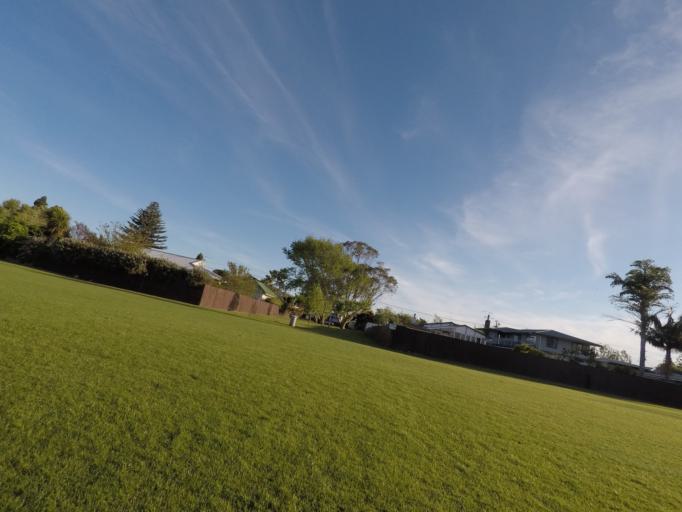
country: NZ
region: Auckland
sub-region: Auckland
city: Rosebank
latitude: -36.8433
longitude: 174.6489
